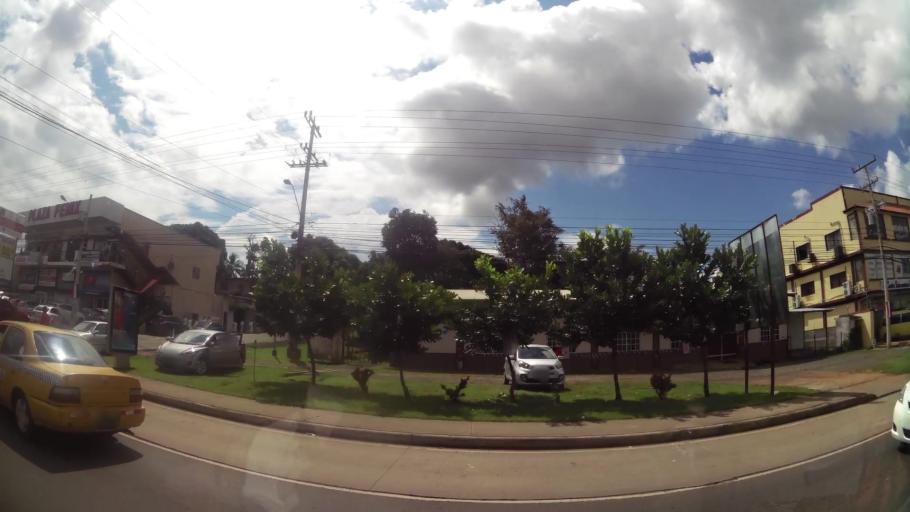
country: PA
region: Panama
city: Nuevo Arraijan
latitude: 8.9263
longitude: -79.7174
